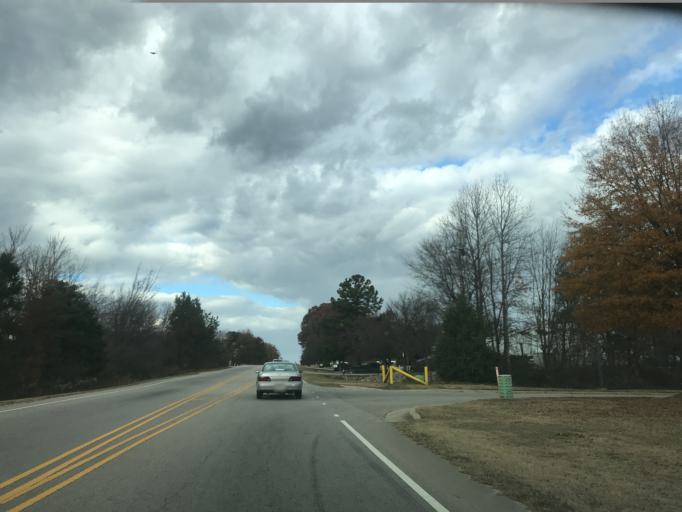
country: US
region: North Carolina
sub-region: Wake County
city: Raleigh
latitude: 35.7916
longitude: -78.5613
